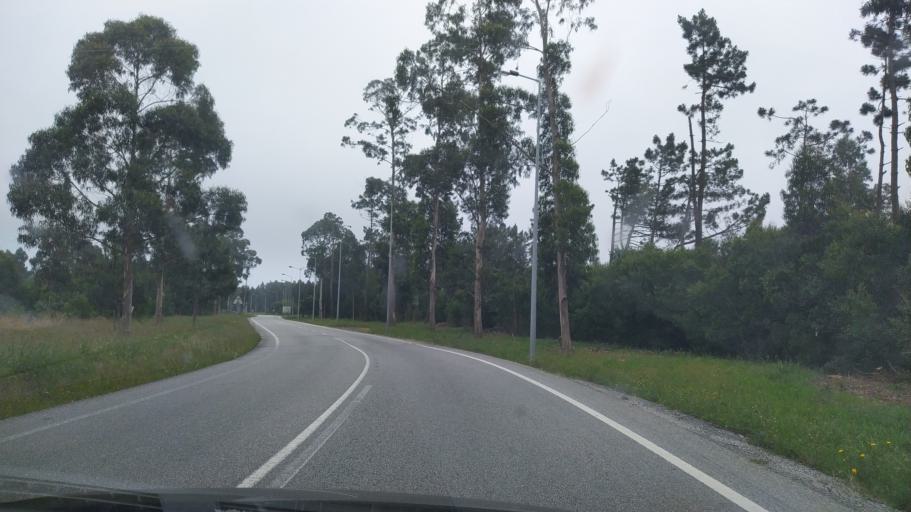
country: PT
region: Aveiro
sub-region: Ilhavo
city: Gafanha da Encarnacao
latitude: 40.6233
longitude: -8.7235
